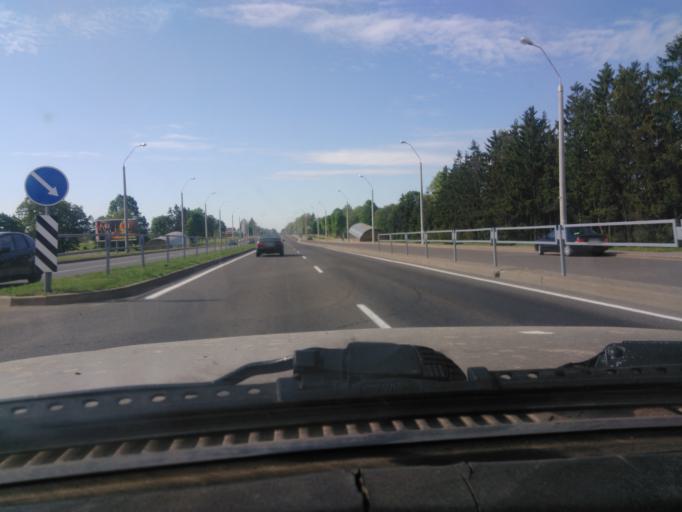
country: BY
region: Mogilev
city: Buynichy
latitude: 53.8629
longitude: 30.2587
